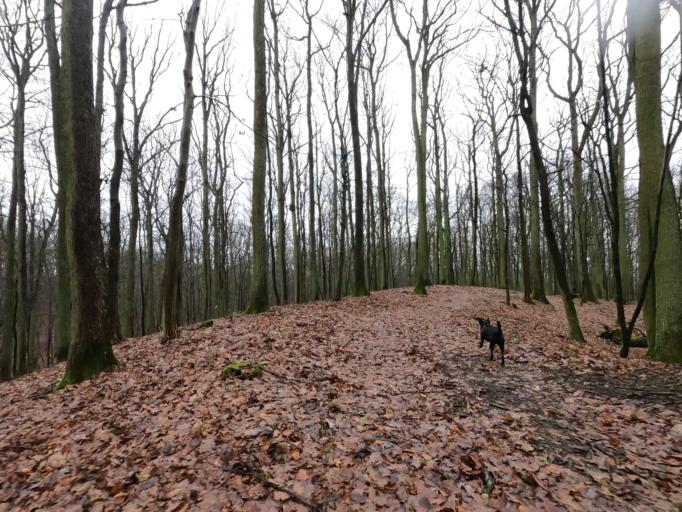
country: PL
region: Greater Poland Voivodeship
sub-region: Powiat pilski
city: Osiek nad Notecia
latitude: 53.1230
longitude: 17.2668
